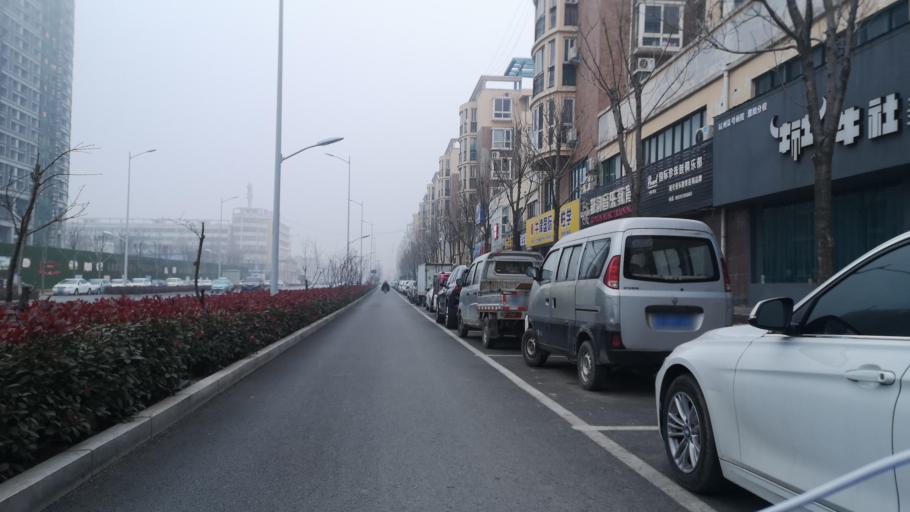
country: CN
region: Henan Sheng
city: Zhongyuanlu
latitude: 35.7645
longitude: 115.0847
